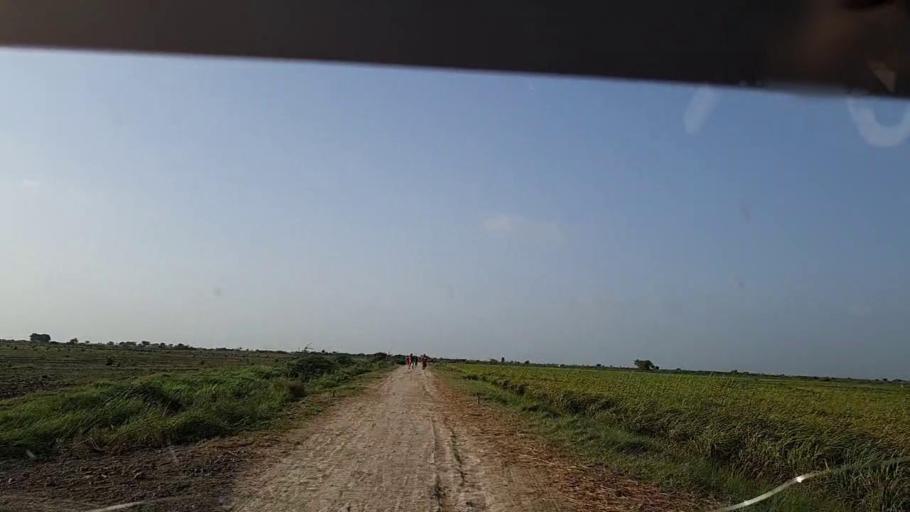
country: PK
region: Sindh
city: Badin
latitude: 24.5612
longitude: 68.8835
